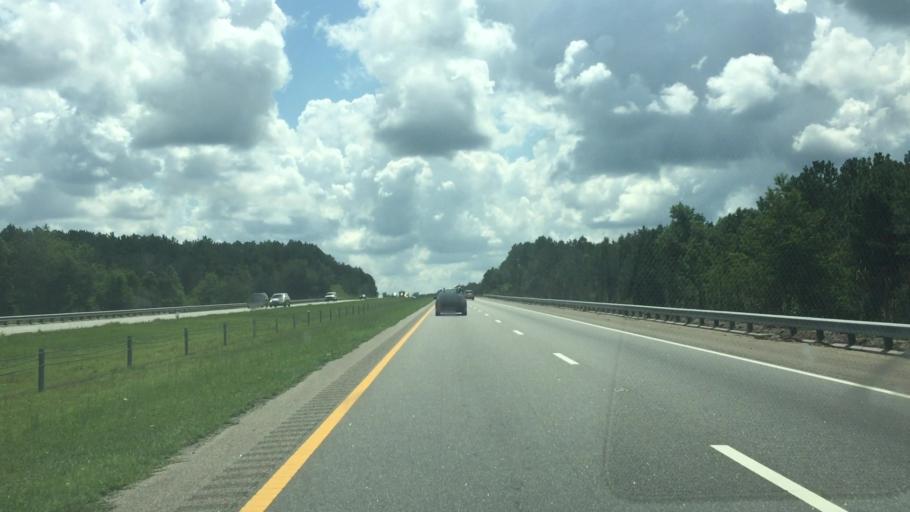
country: US
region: North Carolina
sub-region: Richmond County
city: East Rockingham
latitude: 34.8773
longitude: -79.7731
